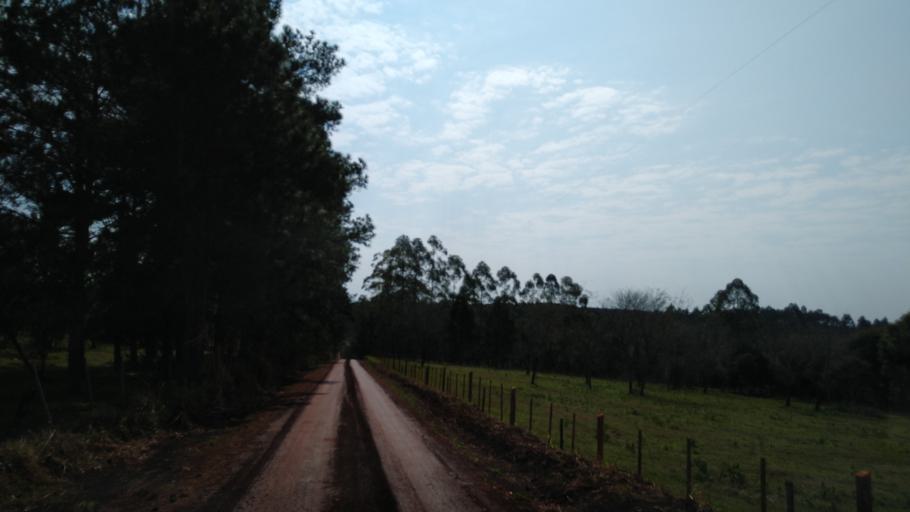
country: AR
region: Misiones
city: Capiovi
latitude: -26.9497
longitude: -55.0442
